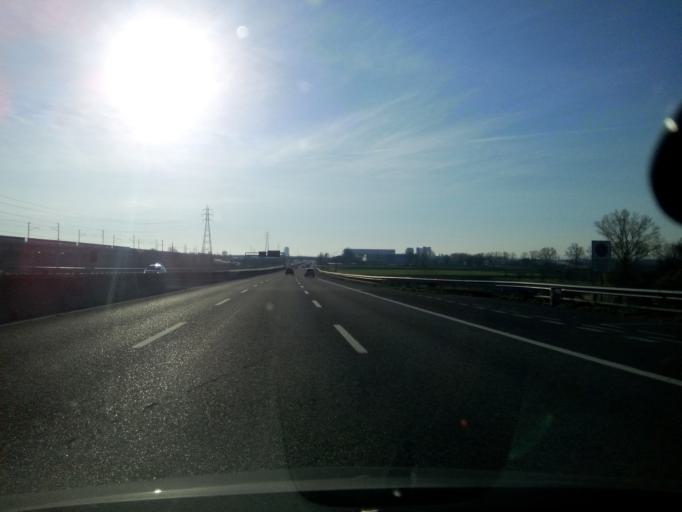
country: IT
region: Emilia-Romagna
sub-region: Provincia di Parma
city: Parma
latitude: 44.8365
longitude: 10.3521
